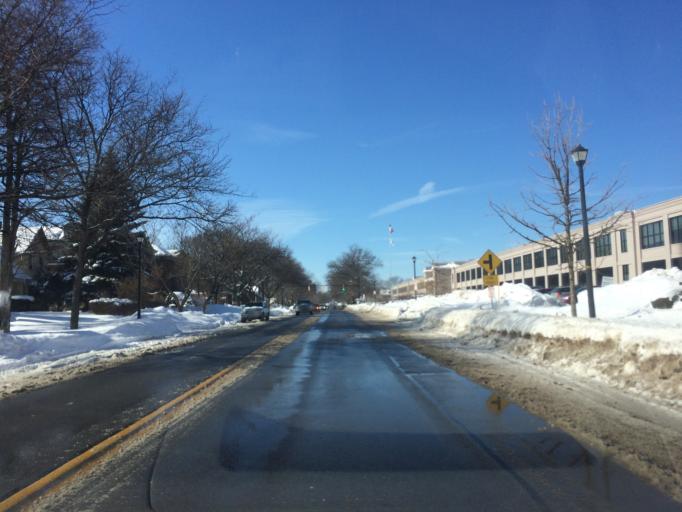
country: US
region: New York
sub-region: Monroe County
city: Brighton
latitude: 43.1527
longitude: -77.5744
